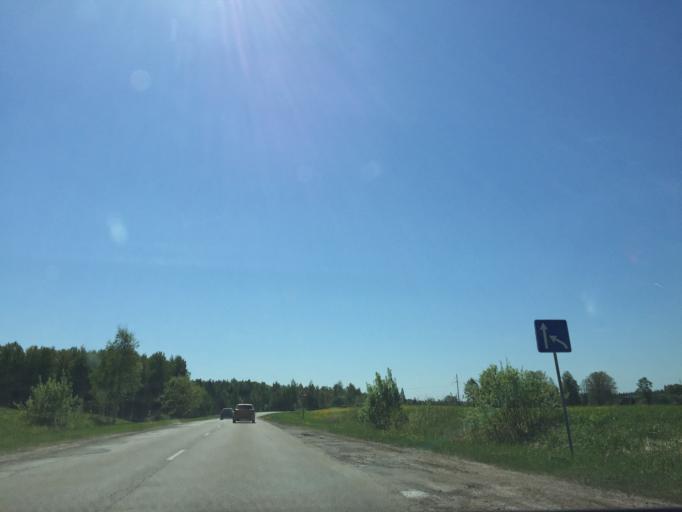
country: LV
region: Malpils
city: Malpils
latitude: 56.9285
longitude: 24.9359
